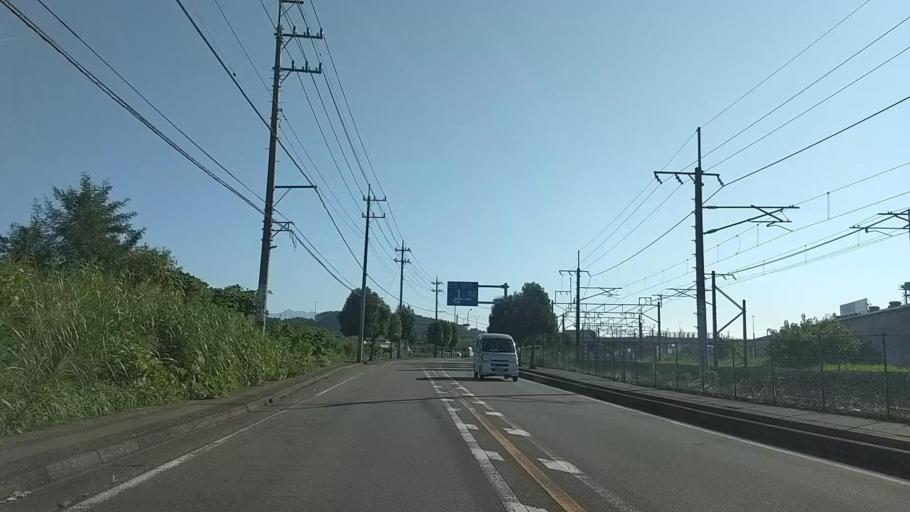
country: JP
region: Gunma
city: Annaka
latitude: 36.3311
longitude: 138.9096
